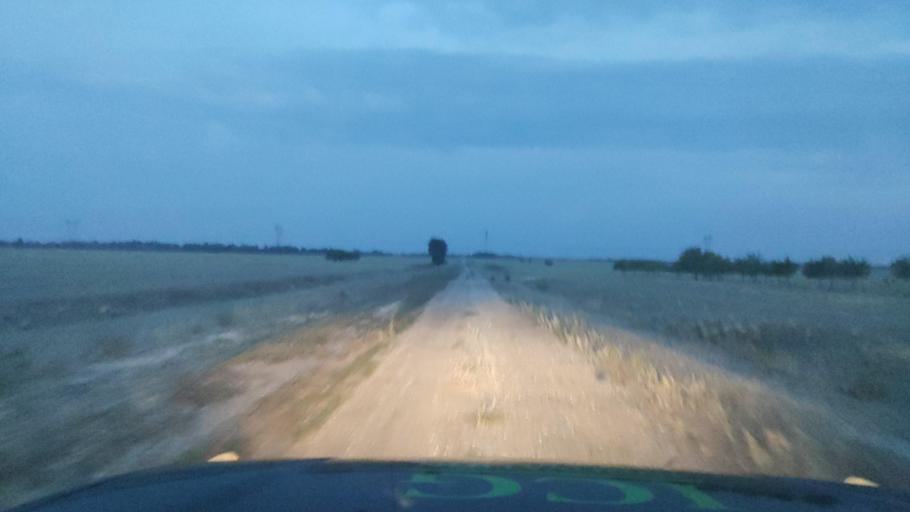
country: KZ
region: Pavlodar
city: Koktobe
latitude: 51.9662
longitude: 77.5920
